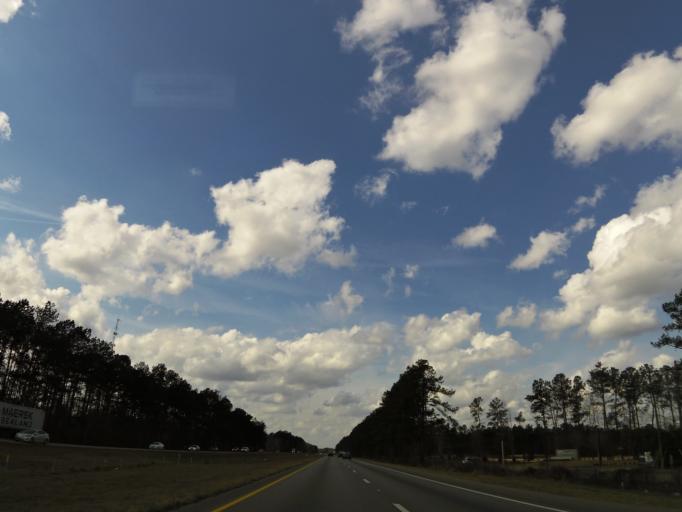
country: US
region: South Carolina
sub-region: Dorchester County
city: Summerville
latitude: 33.0730
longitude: -80.1934
